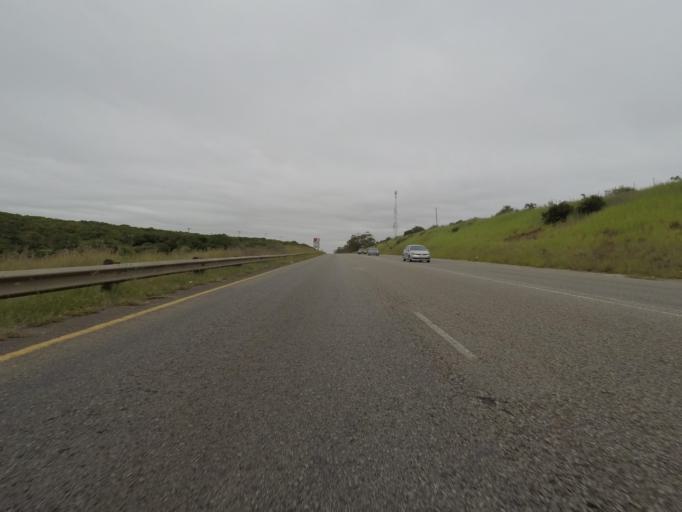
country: ZA
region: Eastern Cape
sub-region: Nelson Mandela Bay Metropolitan Municipality
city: Port Elizabeth
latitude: -33.6850
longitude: 25.8401
